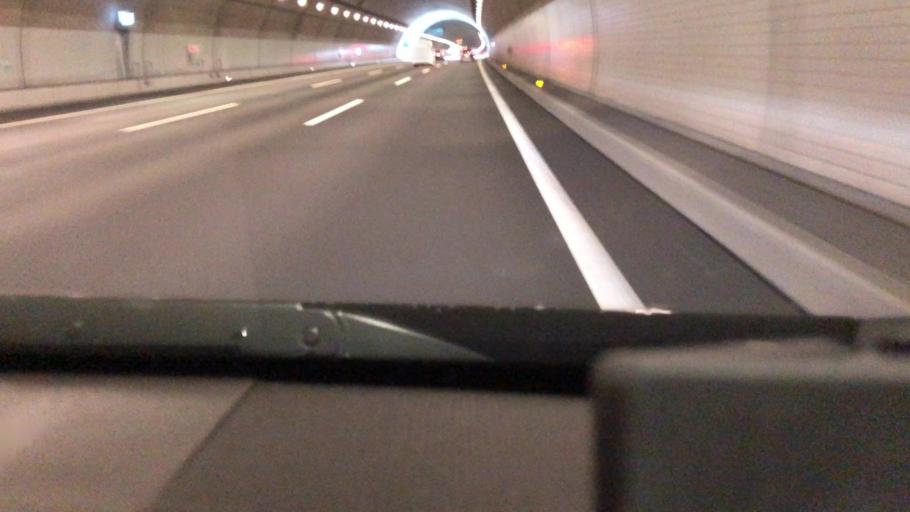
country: JP
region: Shizuoka
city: Shizuoka-shi
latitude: 35.0131
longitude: 138.3249
